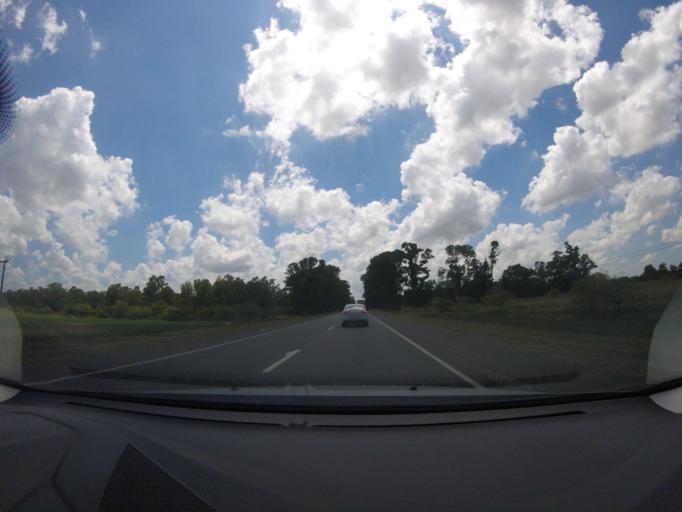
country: AR
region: Buenos Aires
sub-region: Partido de Las Flores
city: Las Flores
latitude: -36.0475
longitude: -59.0873
